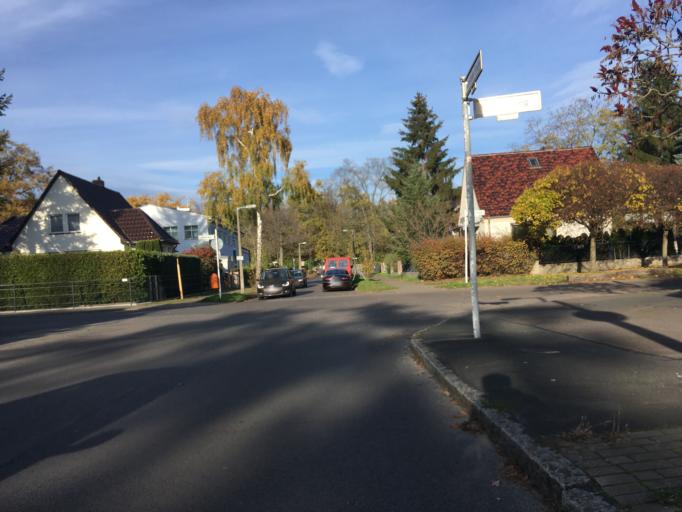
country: DE
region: Berlin
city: Karlshorst
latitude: 52.4915
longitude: 13.5333
